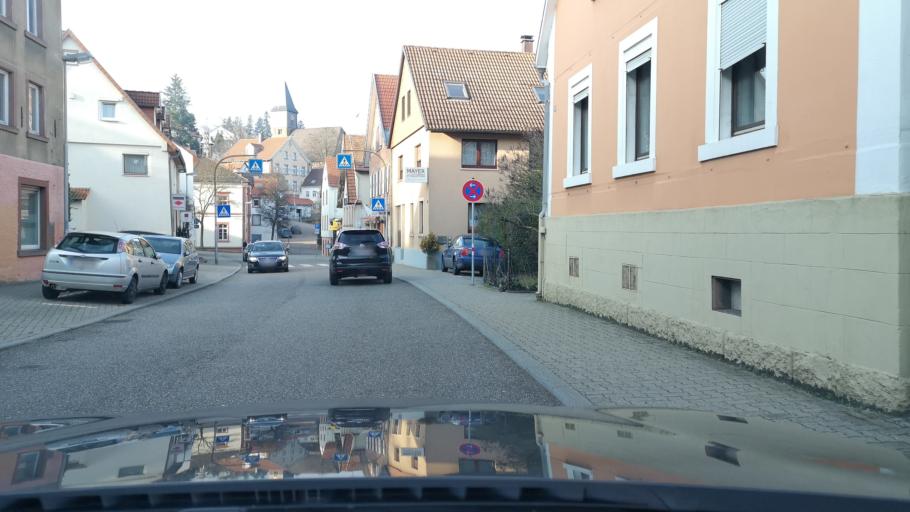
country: DE
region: Baden-Wuerttemberg
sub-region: Karlsruhe Region
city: Ettlingen
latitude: 48.9572
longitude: 8.4677
